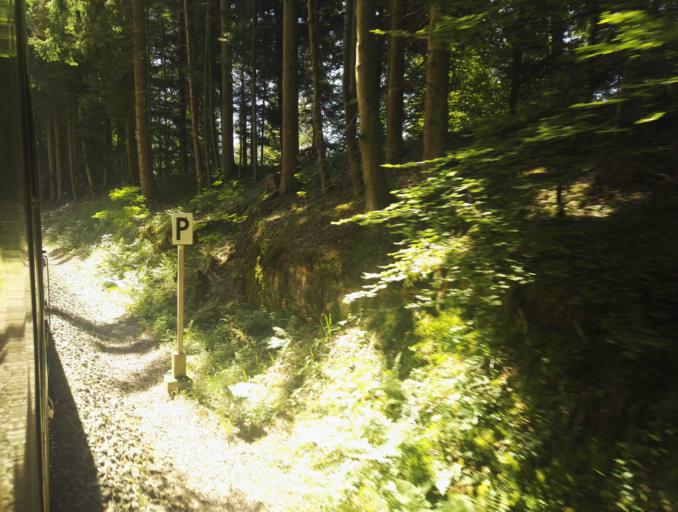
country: DE
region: Baden-Wuerttemberg
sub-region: Regierungsbezirk Stuttgart
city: Welzheim
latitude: 48.8685
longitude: 9.6179
